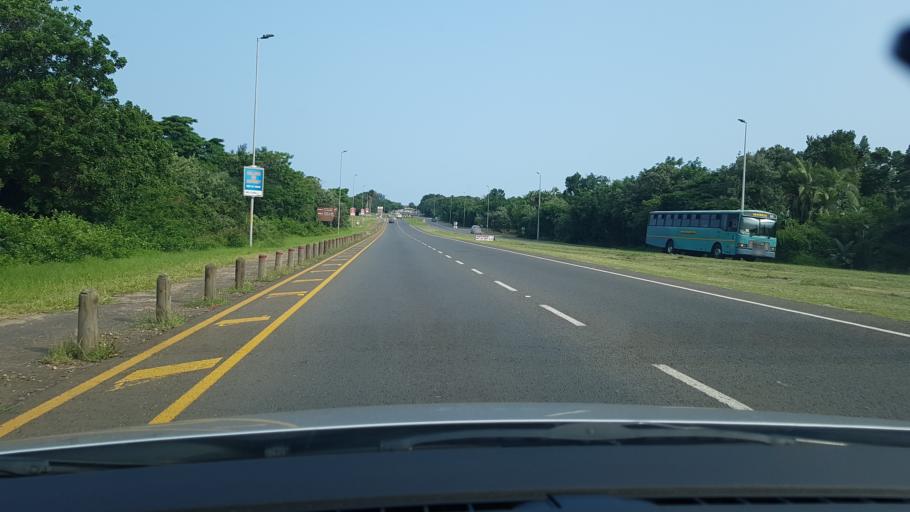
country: ZA
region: KwaZulu-Natal
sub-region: uThungulu District Municipality
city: Richards Bay
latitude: -28.7848
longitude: 32.0873
